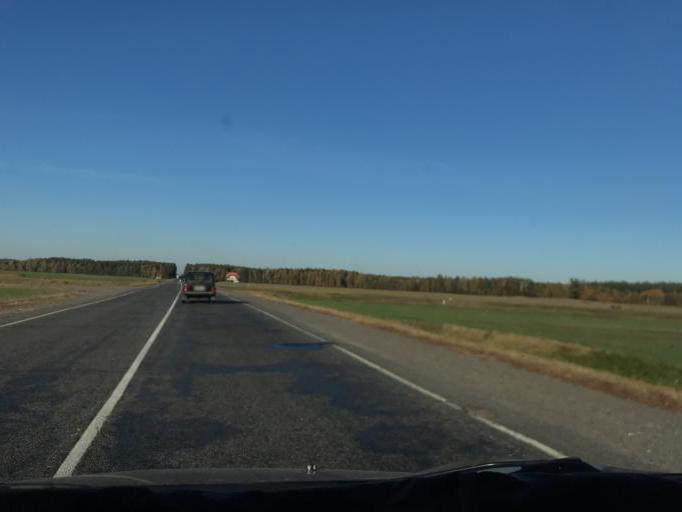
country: BY
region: Gomel
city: Kalinkavichy
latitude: 52.0463
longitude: 29.3612
